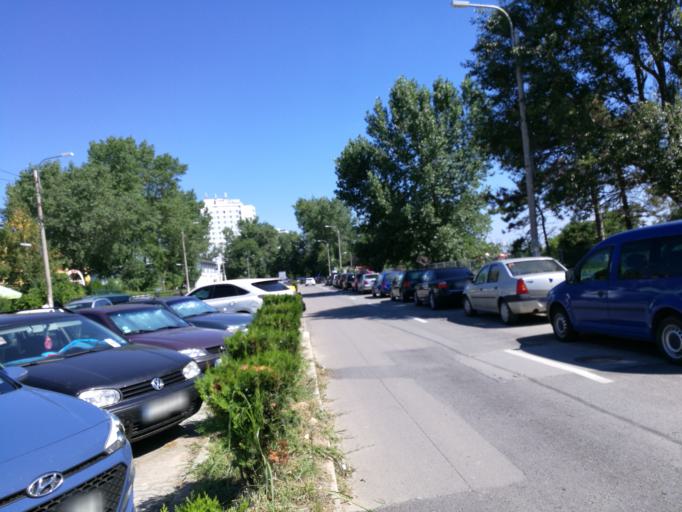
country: RO
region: Constanta
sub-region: Oras Eforie
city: Eforie Nord
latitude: 44.0721
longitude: 28.6377
